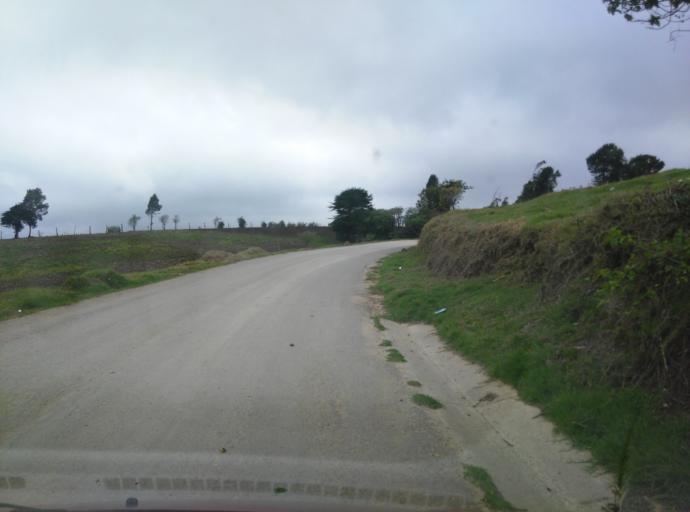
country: CO
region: Boyaca
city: Siachoque
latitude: 5.4926
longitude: -73.2878
